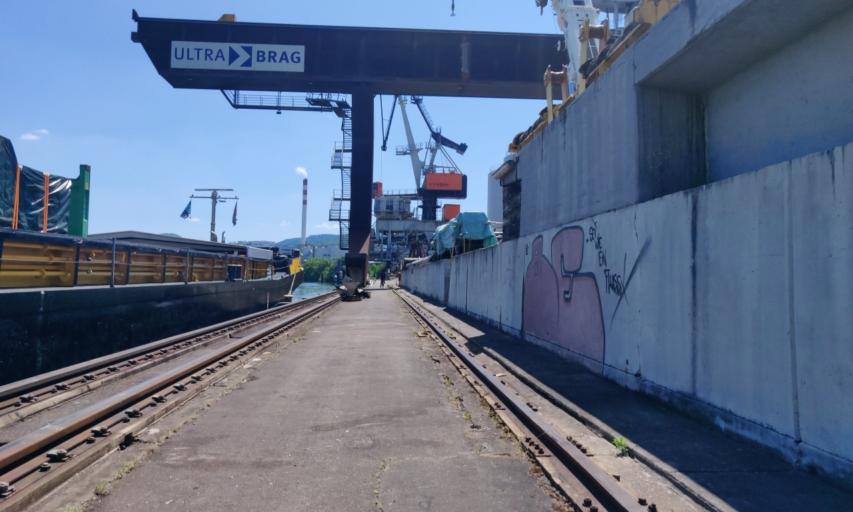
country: DE
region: Baden-Wuerttemberg
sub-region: Freiburg Region
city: Grenzach-Wyhlen
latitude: 47.5406
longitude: 7.6620
